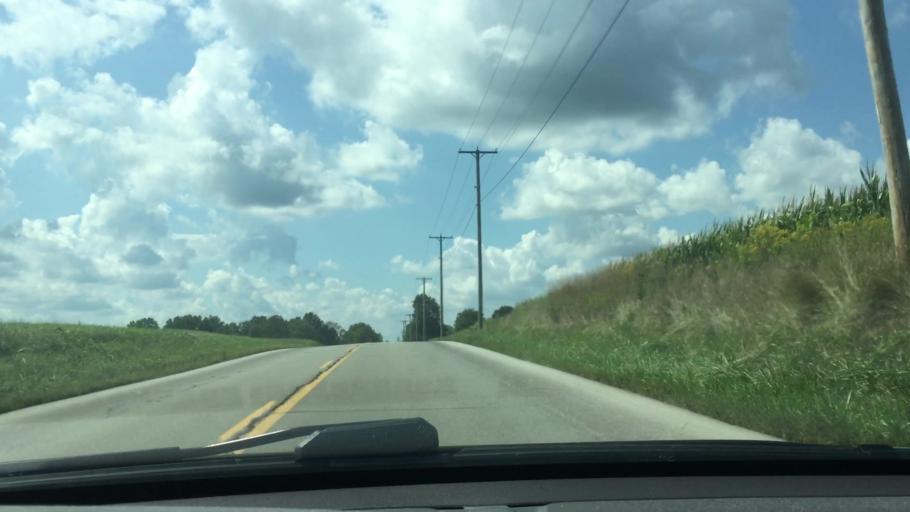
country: US
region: Pennsylvania
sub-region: Lawrence County
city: New Wilmington
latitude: 41.1204
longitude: -80.3914
